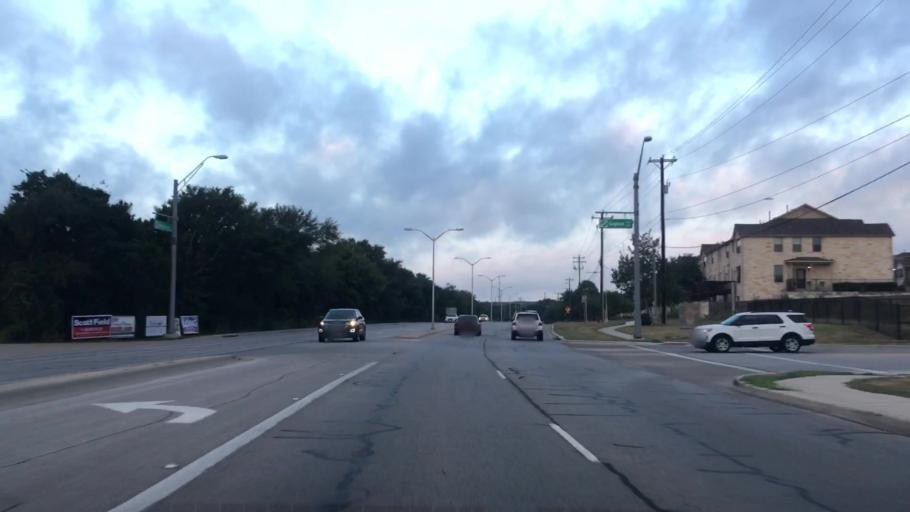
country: US
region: Texas
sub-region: Williamson County
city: Cedar Park
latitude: 30.5071
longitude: -97.7951
